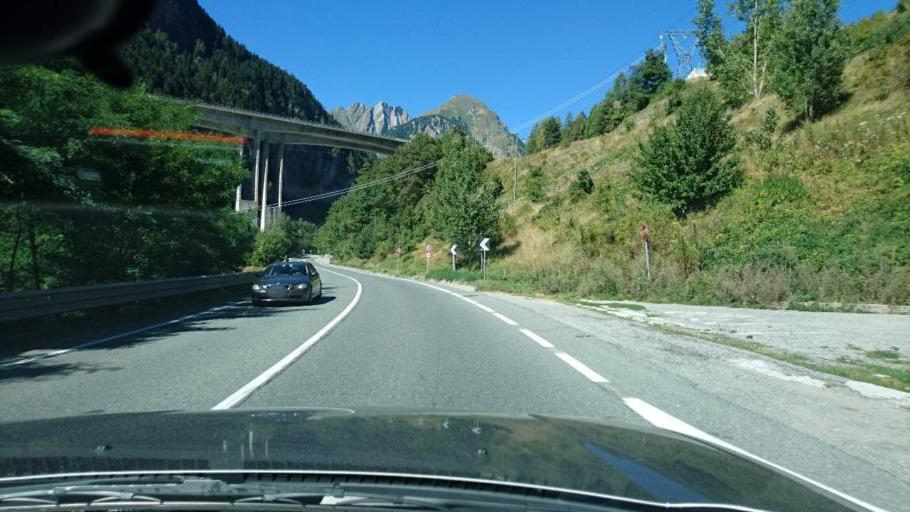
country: IT
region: Aosta Valley
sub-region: Valle d'Aosta
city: Morgex
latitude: 45.7607
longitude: 7.0207
